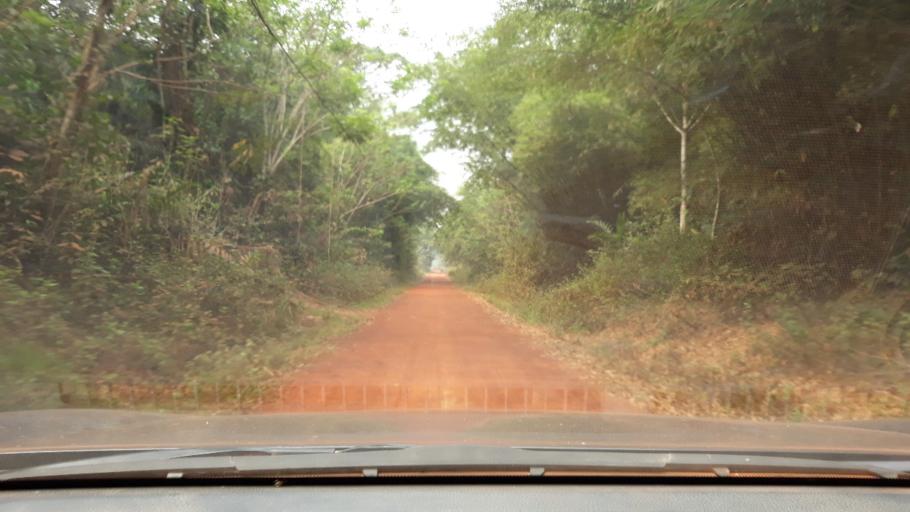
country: CD
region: Eastern Province
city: Aketi
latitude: 2.9351
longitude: 24.0961
